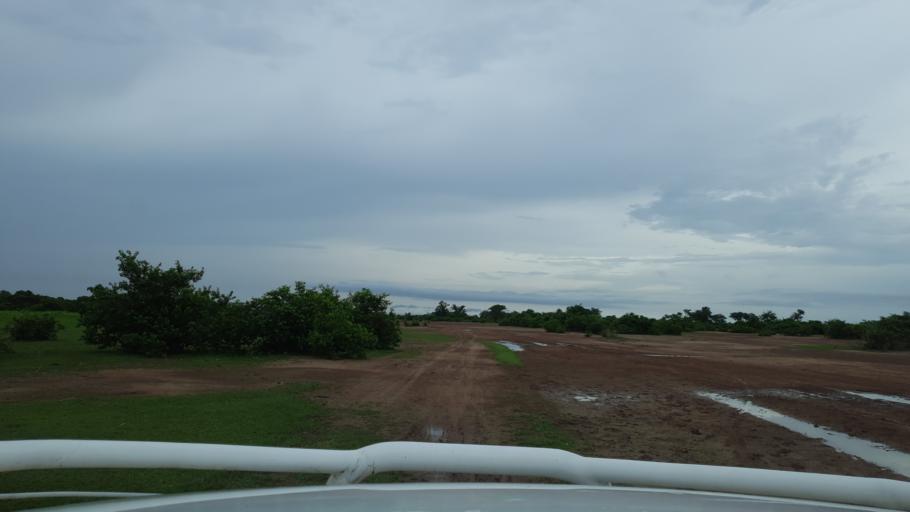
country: ML
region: Segou
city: Bla
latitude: 12.7464
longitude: -5.6354
